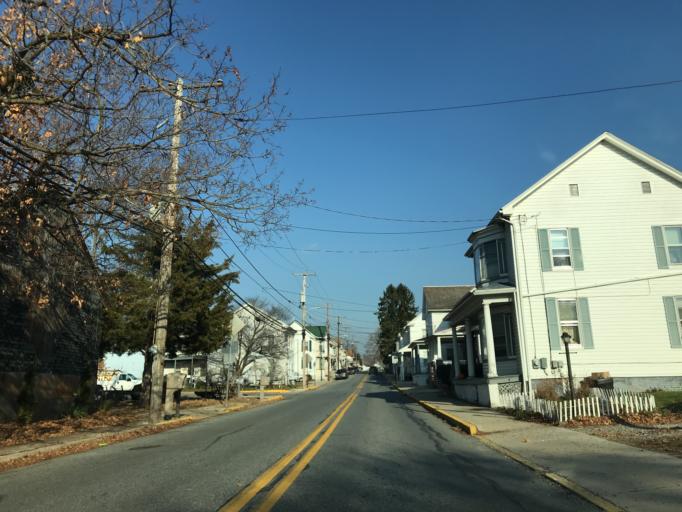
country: US
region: Pennsylvania
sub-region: York County
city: Loganville
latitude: 39.8543
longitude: -76.7705
